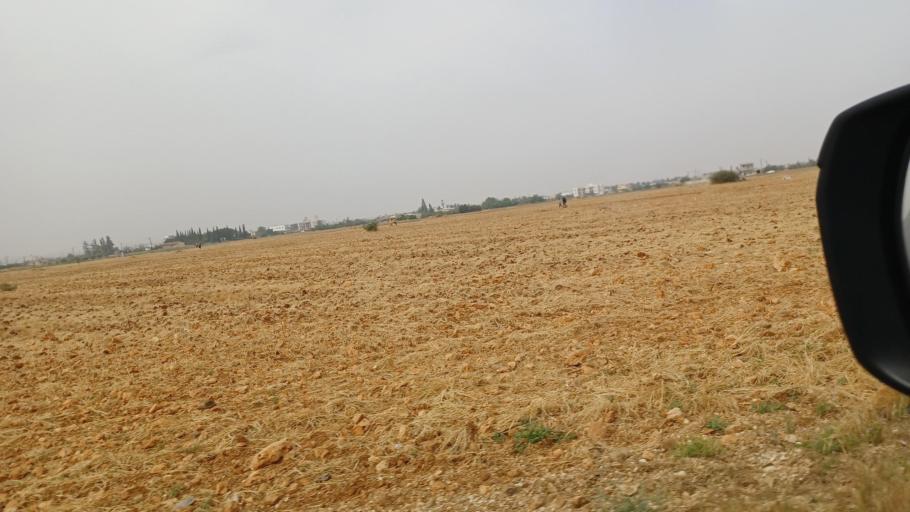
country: CY
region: Lefkosia
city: Kokkinotrimithia
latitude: 35.1542
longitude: 33.2194
